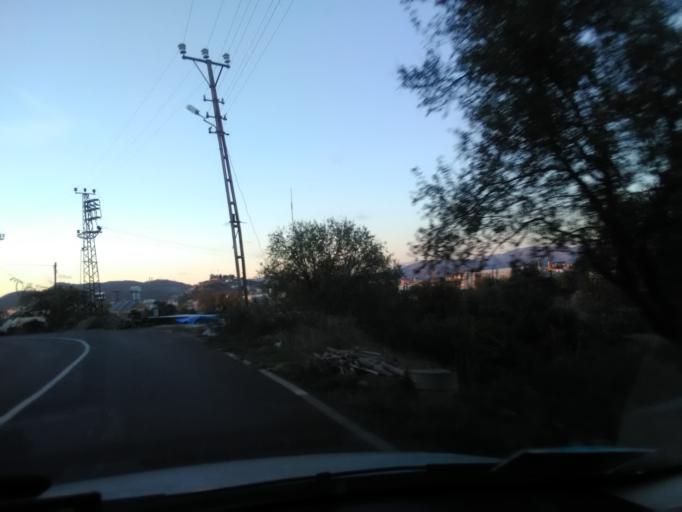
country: TR
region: Antalya
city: Gazipasa
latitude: 36.2593
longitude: 32.3173
